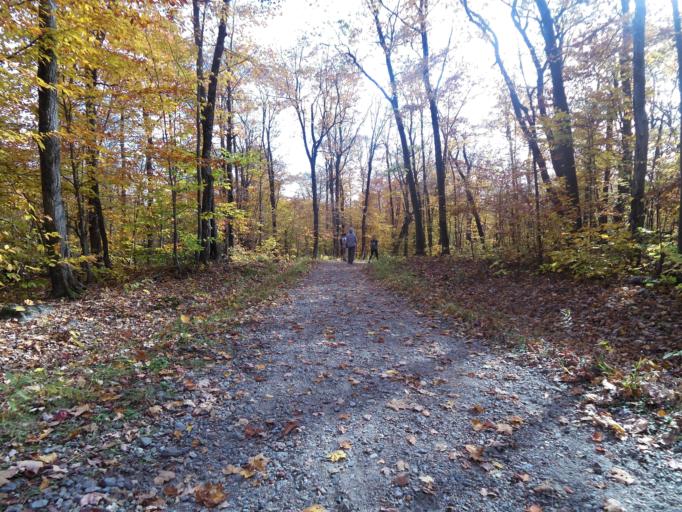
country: CA
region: Quebec
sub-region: Outaouais
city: Gatineau
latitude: 45.4988
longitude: -75.8456
